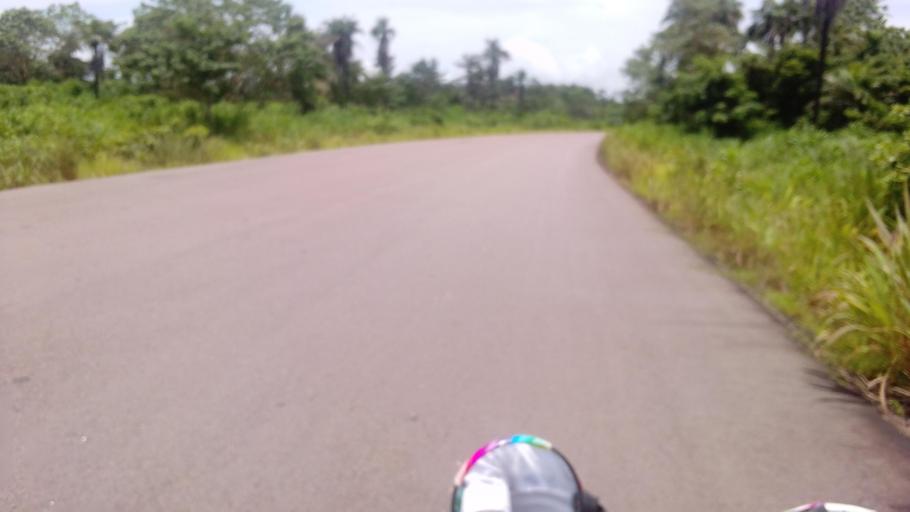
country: SL
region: Northern Province
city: Makeni
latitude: 9.0579
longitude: -12.1765
